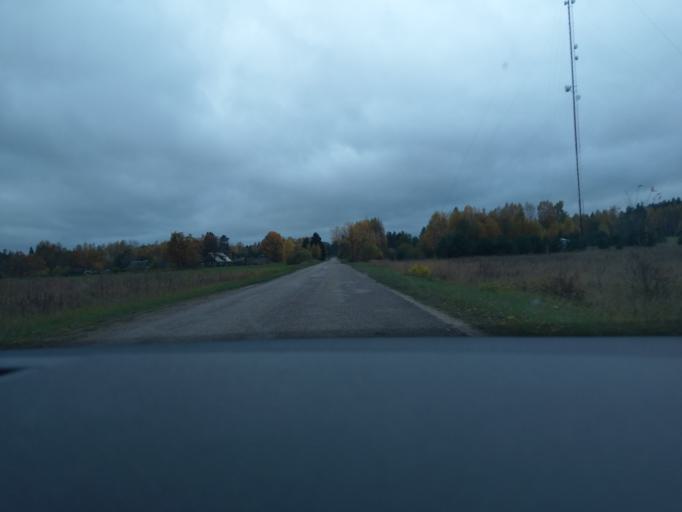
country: LV
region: Talsu Rajons
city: Stende
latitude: 57.0793
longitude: 22.2831
